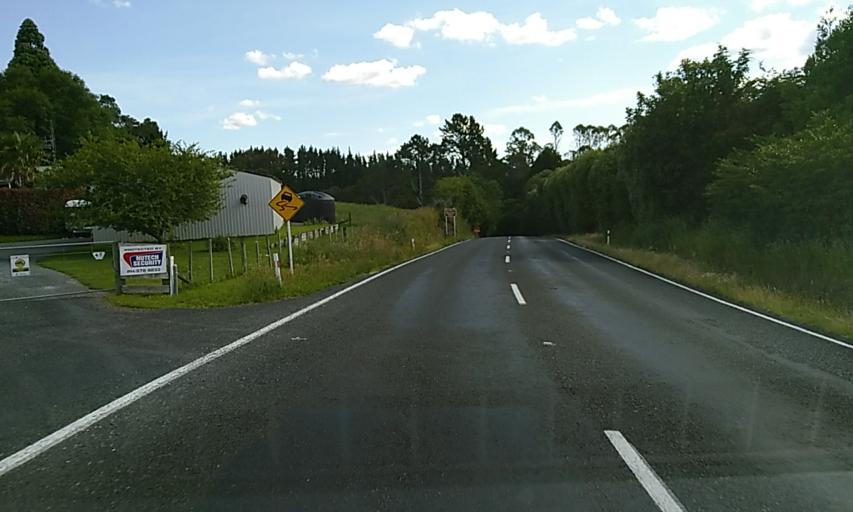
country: NZ
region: Bay of Plenty
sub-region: Tauranga City
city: Tauranga
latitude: -37.8031
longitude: 176.0435
